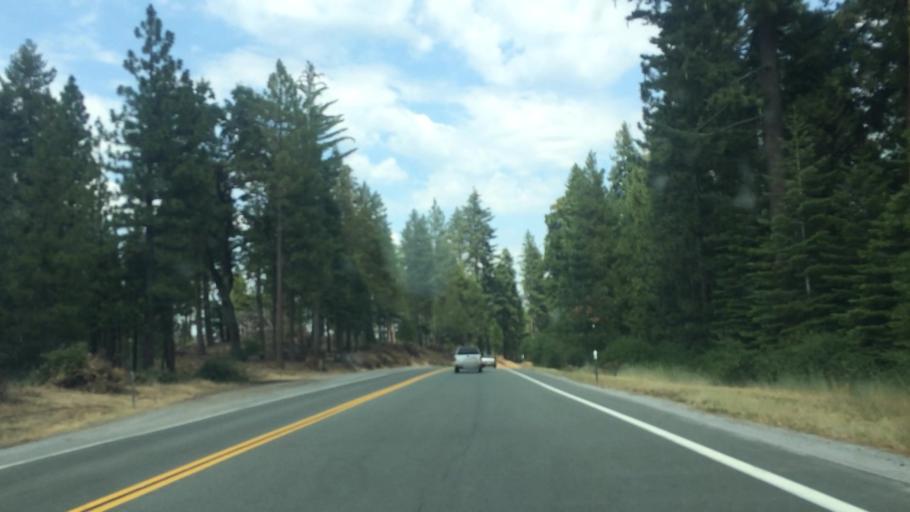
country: US
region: California
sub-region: Amador County
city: Pioneer
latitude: 38.5152
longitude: -120.4623
